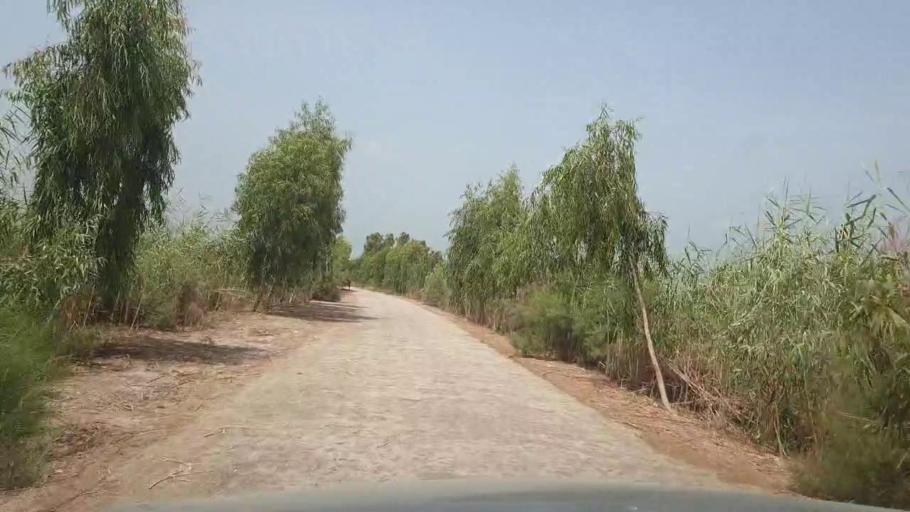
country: PK
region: Sindh
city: Garhi Yasin
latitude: 27.9468
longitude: 68.3714
